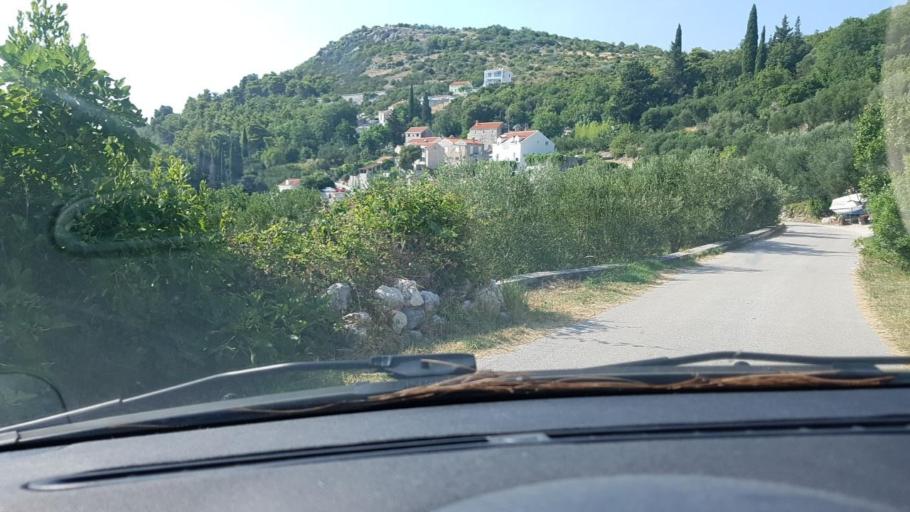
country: HR
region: Dubrovacko-Neretvanska
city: Podgora
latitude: 42.7831
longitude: 17.8619
